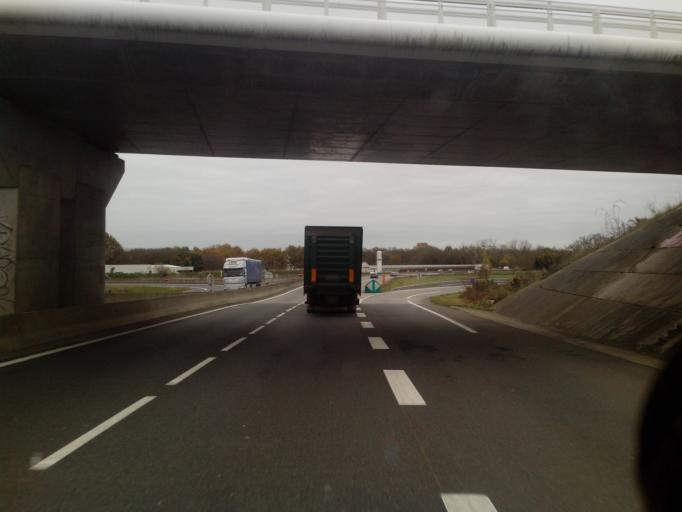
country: FR
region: Pays de la Loire
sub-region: Departement de la Loire-Atlantique
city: Basse-Goulaine
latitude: 47.2278
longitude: -1.4675
